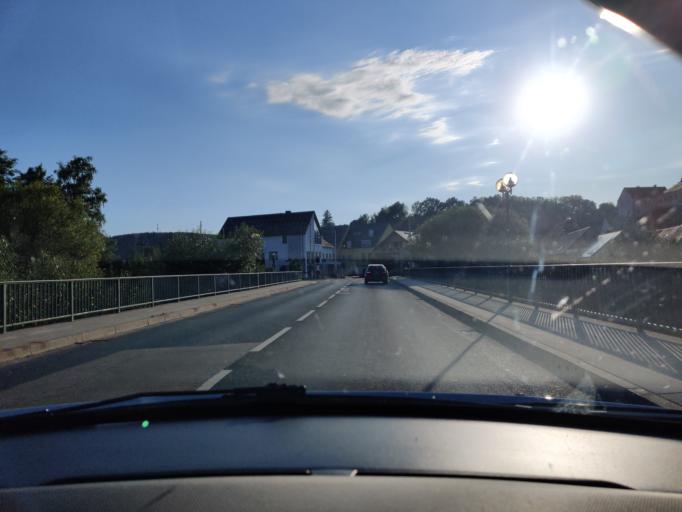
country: DE
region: Bavaria
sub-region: Upper Palatinate
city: Nabburg
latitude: 49.4522
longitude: 12.1843
